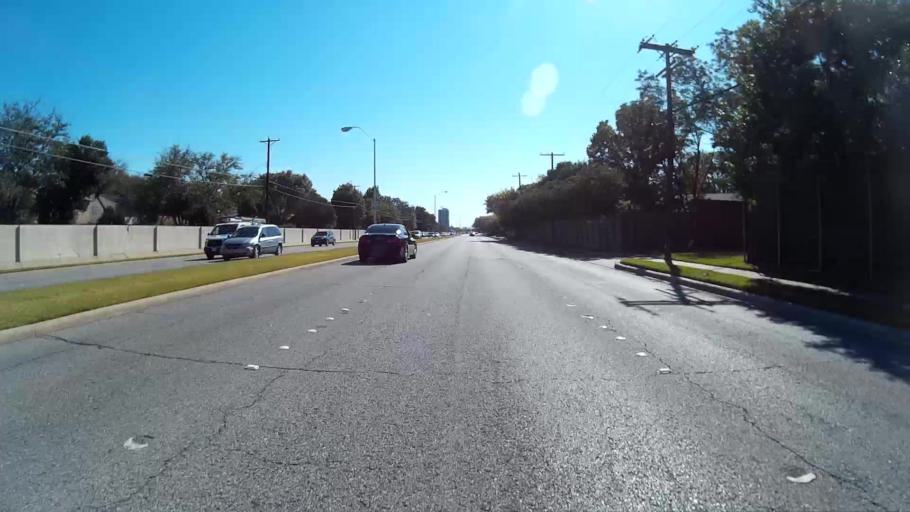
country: US
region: Texas
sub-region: Dallas County
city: Richardson
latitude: 32.9667
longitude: -96.7690
